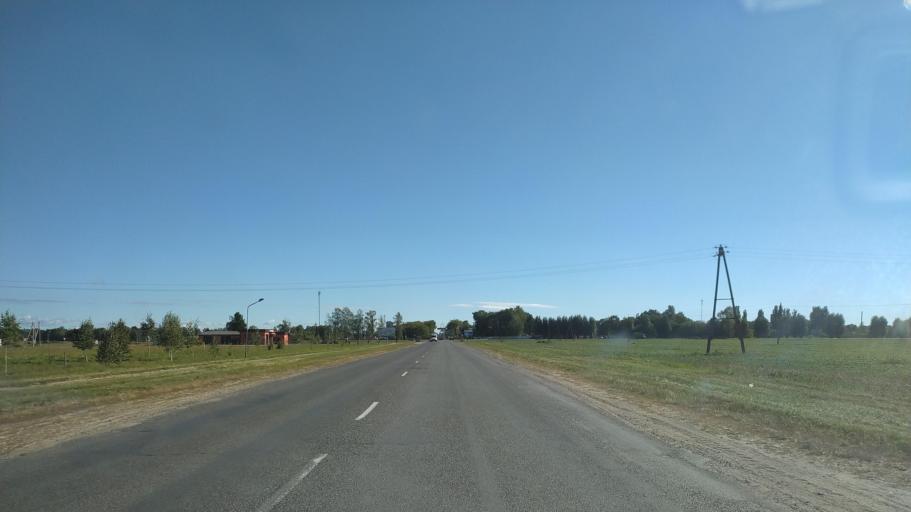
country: BY
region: Brest
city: Byaroza
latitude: 52.5251
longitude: 24.9483
